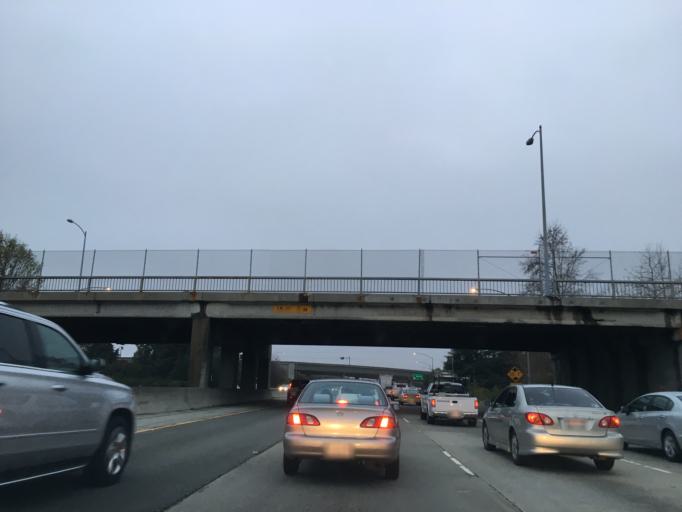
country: US
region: California
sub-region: Santa Clara County
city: Mountain View
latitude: 37.4076
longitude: -122.0658
